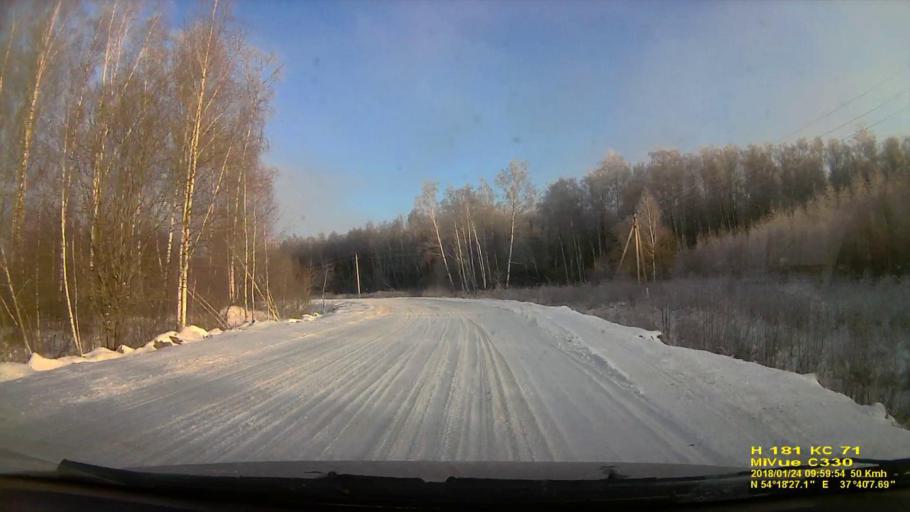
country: RU
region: Tula
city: Revyakino
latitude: 54.3076
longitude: 37.6689
